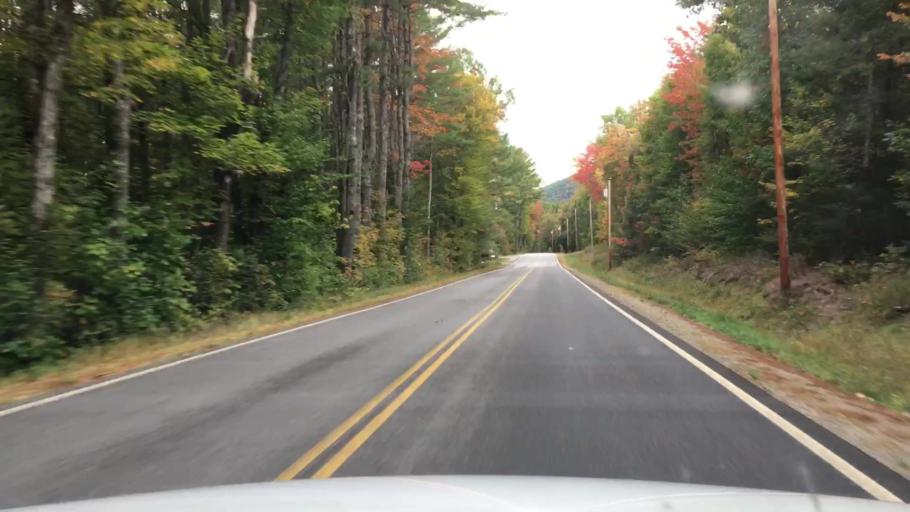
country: US
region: Maine
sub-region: Oxford County
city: Bethel
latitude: 44.2668
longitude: -70.7277
